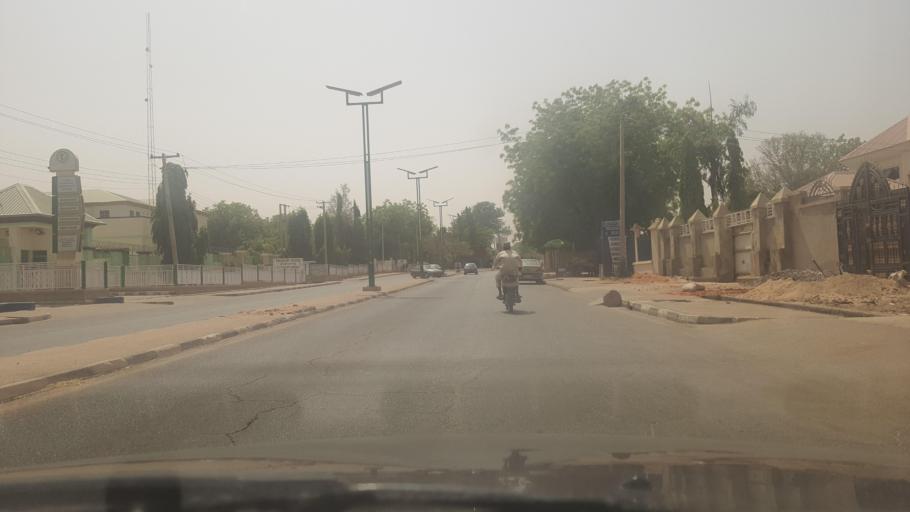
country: NG
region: Gombe
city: Gombe
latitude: 10.2827
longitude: 11.1549
